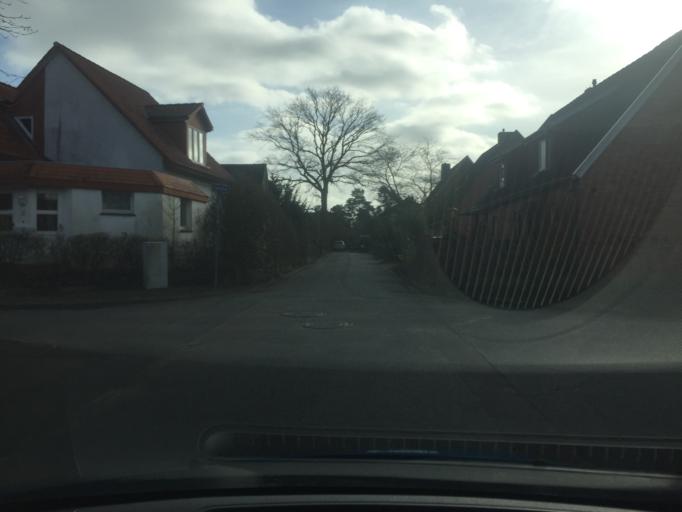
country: DE
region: Lower Saxony
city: Lueneburg
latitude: 53.2341
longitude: 10.4295
